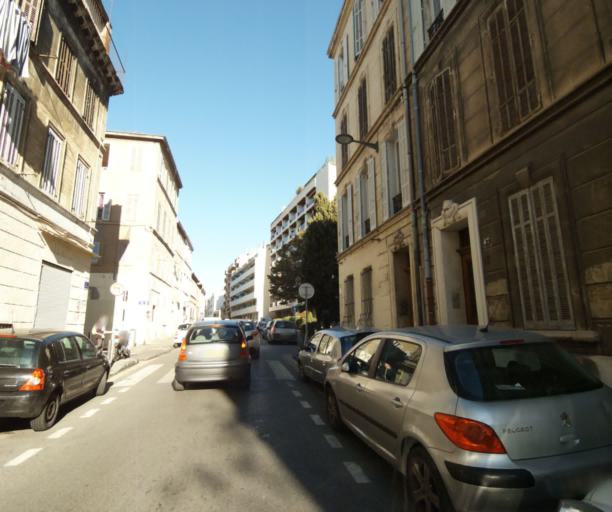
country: FR
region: Provence-Alpes-Cote d'Azur
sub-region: Departement des Bouches-du-Rhone
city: Marseille 05
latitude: 43.2860
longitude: 5.3949
